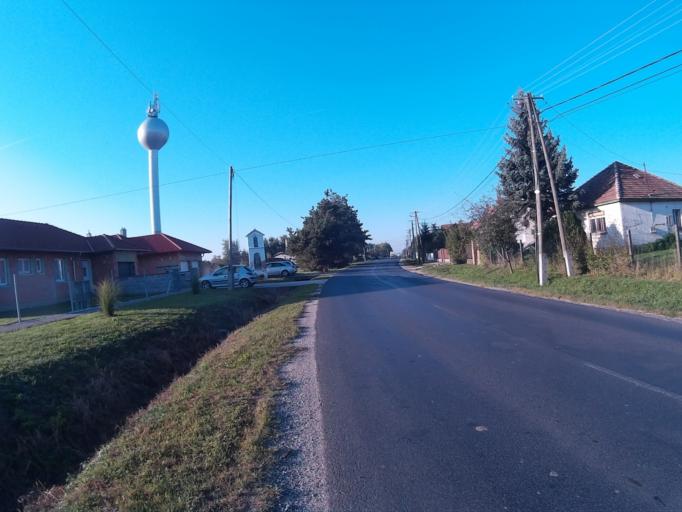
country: HU
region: Vas
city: Jak
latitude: 47.1339
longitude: 16.5840
